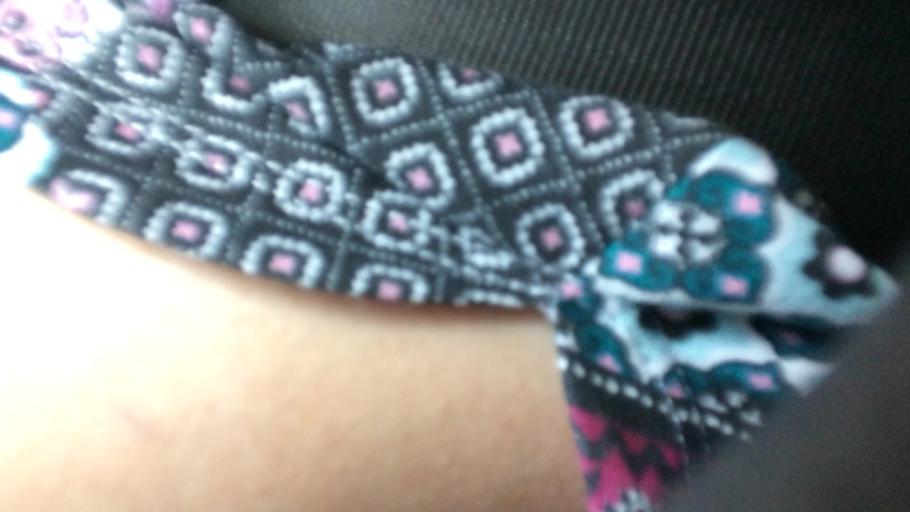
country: US
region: New Mexico
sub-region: Colfax County
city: Springer
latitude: 36.2158
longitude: -104.6599
